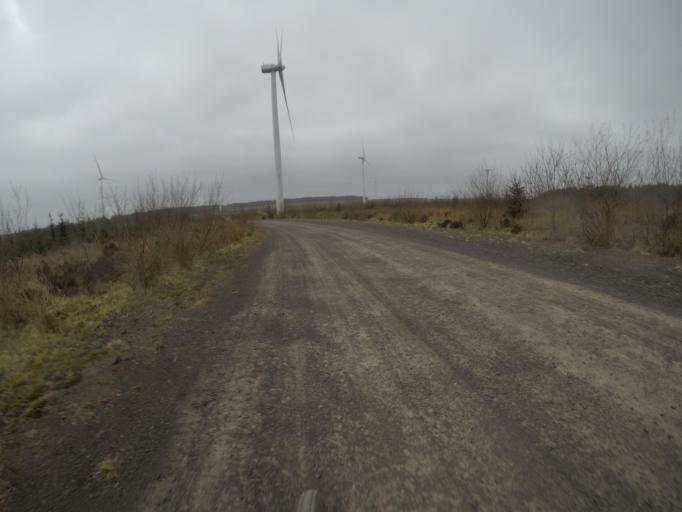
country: GB
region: Scotland
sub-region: East Ayrshire
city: Newmilns
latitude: 55.6501
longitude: -4.3255
